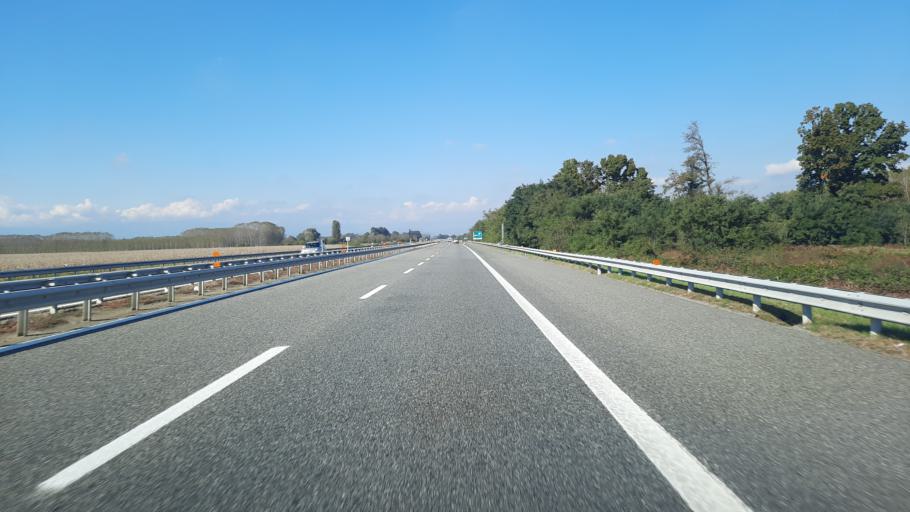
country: IT
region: Piedmont
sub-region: Provincia di Novara
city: Landiona
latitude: 45.4974
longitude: 8.4390
